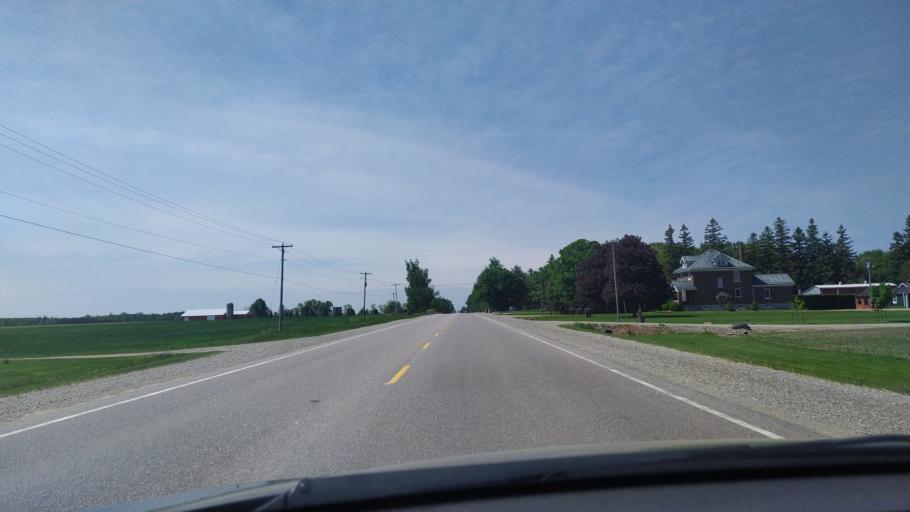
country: CA
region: Ontario
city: Stratford
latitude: 43.3344
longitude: -81.0141
